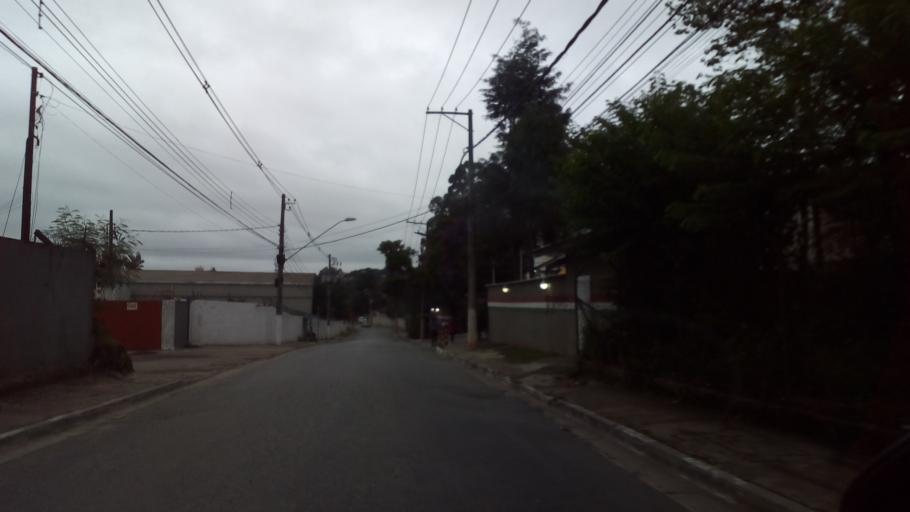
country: BR
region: Sao Paulo
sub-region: Itaquaquecetuba
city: Itaquaquecetuba
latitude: -23.4260
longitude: -46.4112
